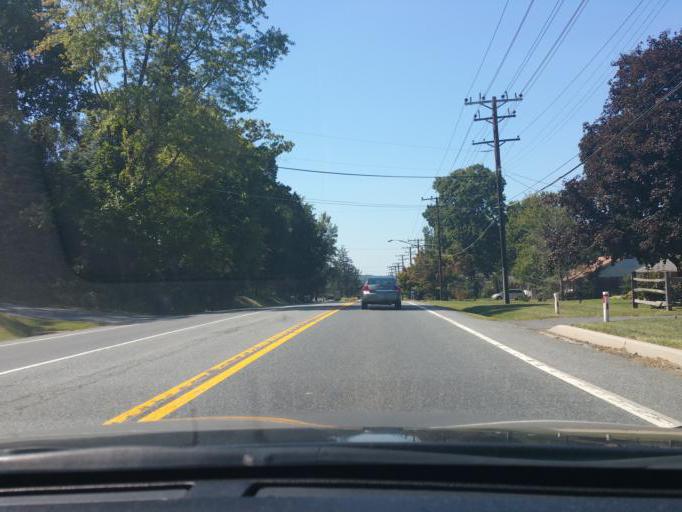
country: US
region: Maryland
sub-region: Harford County
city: South Bel Air
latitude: 39.5491
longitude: -76.3043
